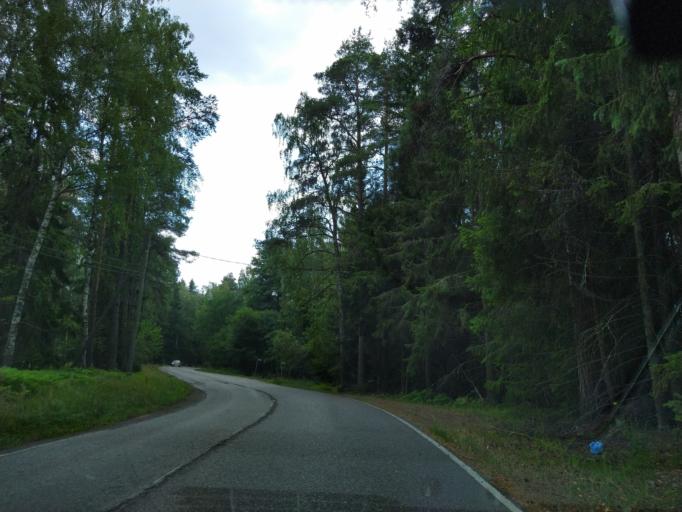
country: FI
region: Uusimaa
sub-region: Helsinki
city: Kirkkonummi
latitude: 60.0778
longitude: 24.5011
